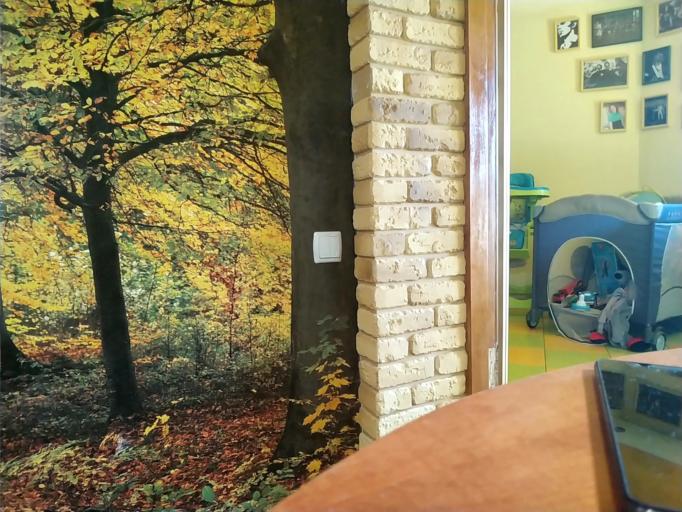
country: RU
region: Tverskaya
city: Krasnomayskiy
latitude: 57.5291
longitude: 34.1581
